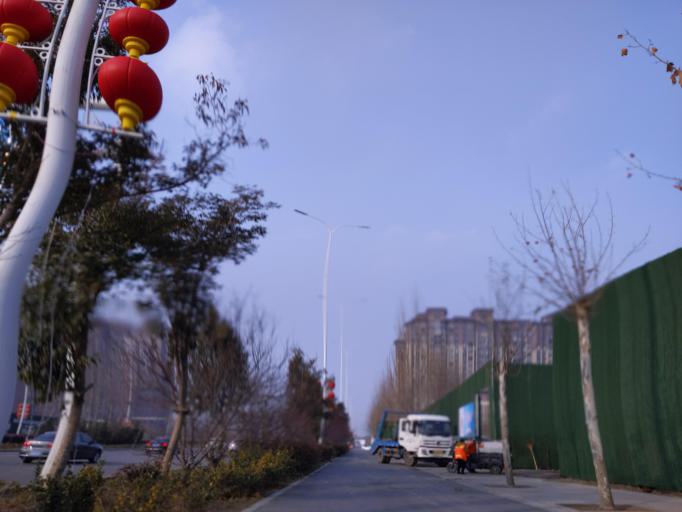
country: CN
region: Henan Sheng
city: Puyang
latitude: 35.8121
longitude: 115.0225
